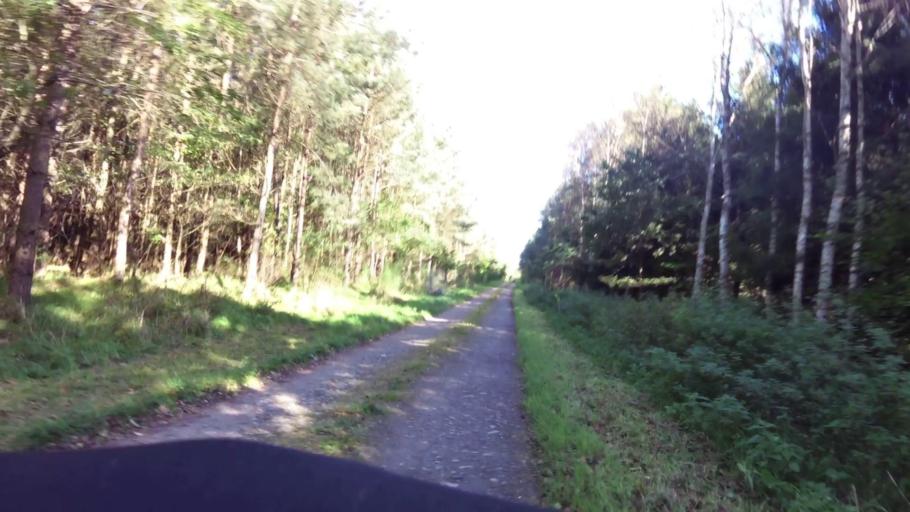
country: PL
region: West Pomeranian Voivodeship
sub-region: Powiat bialogardzki
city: Bialogard
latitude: 53.9941
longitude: 16.1165
